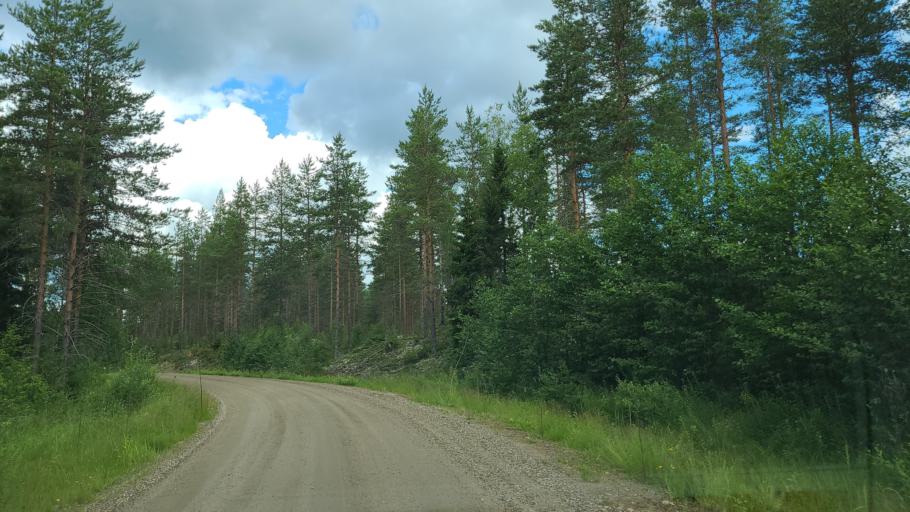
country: FI
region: Northern Savo
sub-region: Koillis-Savo
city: Kaavi
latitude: 63.0311
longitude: 28.7855
